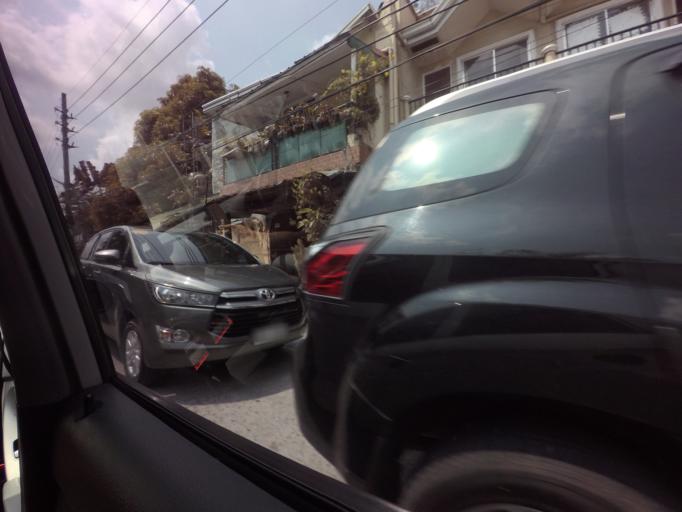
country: PH
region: Metro Manila
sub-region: San Juan
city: San Juan
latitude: 14.5974
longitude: 121.0239
